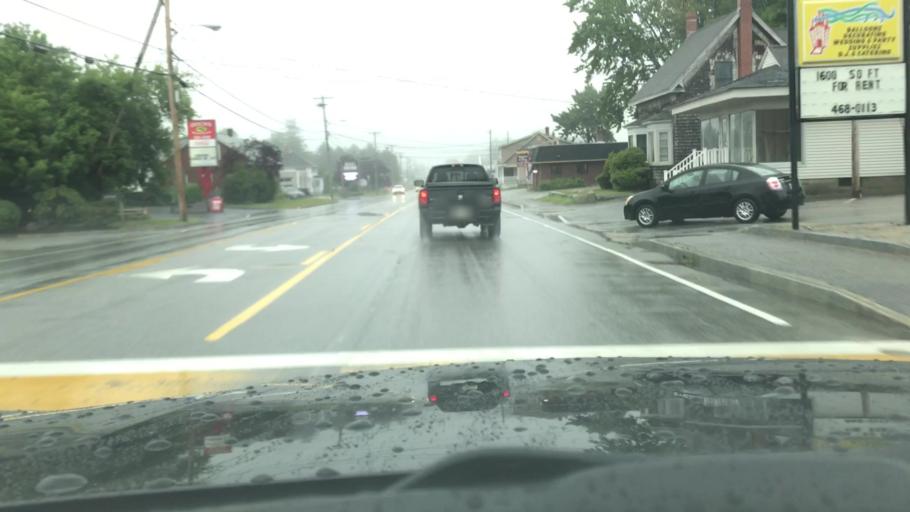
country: US
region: Maine
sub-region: York County
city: Biddeford
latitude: 43.4772
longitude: -70.4769
